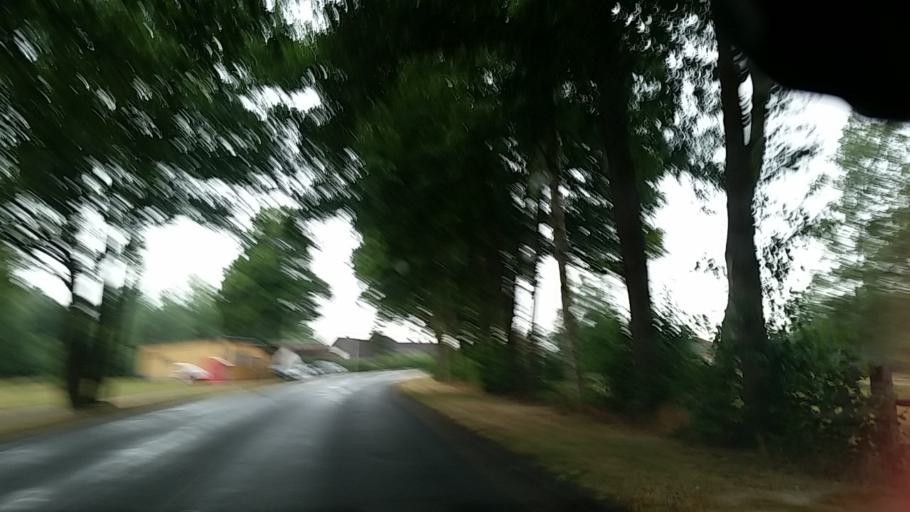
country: DE
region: Lower Saxony
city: Bokensdorf
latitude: 52.4991
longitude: 10.7158
